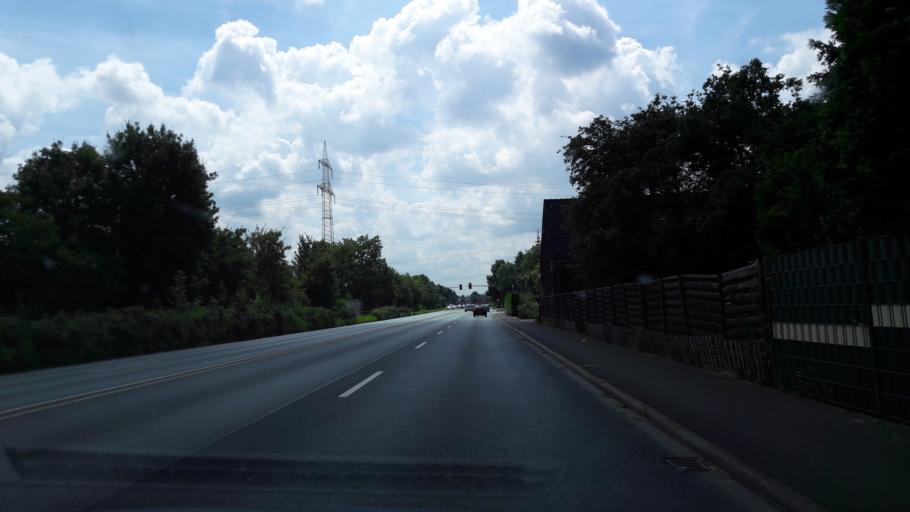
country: DE
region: North Rhine-Westphalia
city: Kamen
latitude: 51.5745
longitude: 7.6710
